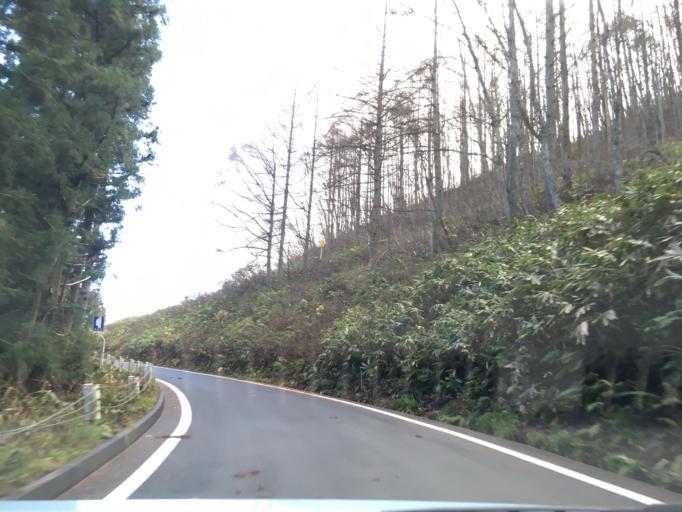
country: JP
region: Fukushima
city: Inawashiro
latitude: 37.4566
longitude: 139.9971
